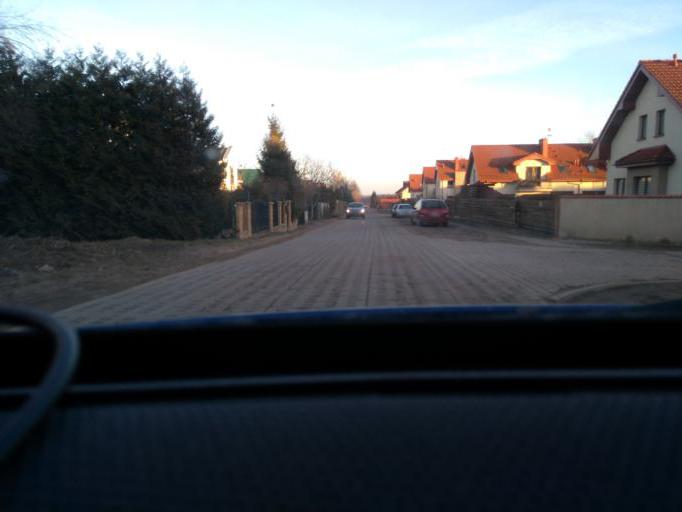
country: PL
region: Pomeranian Voivodeship
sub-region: Powiat kartuski
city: Banino
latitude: 54.3835
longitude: 18.3927
